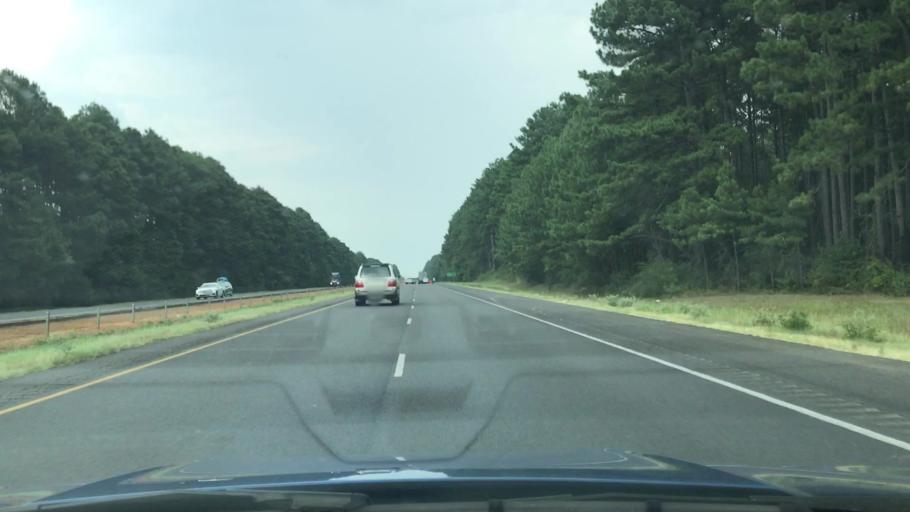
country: US
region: Texas
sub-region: Harrison County
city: Marshall
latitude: 32.4941
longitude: -94.2841
